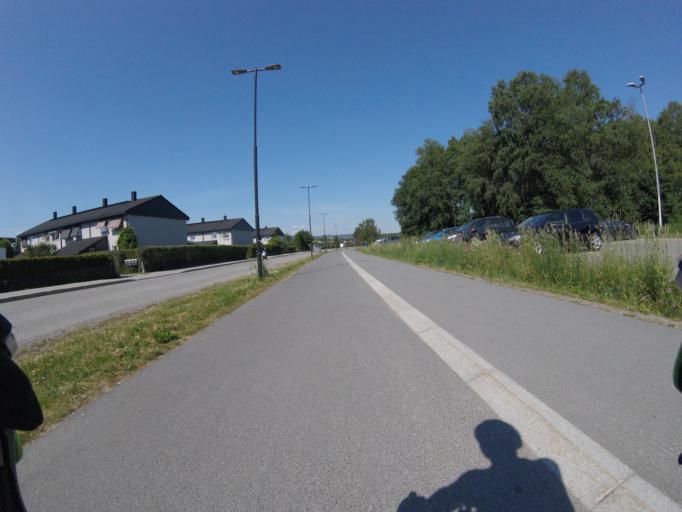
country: NO
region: Akershus
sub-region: Skedsmo
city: Lillestrom
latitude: 59.9641
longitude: 11.0429
